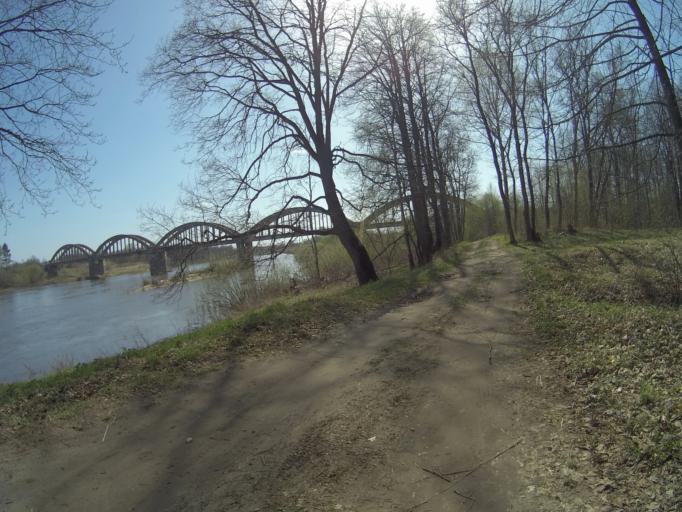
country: RU
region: Vladimir
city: Raduzhnyy
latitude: 56.0552
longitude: 40.3743
